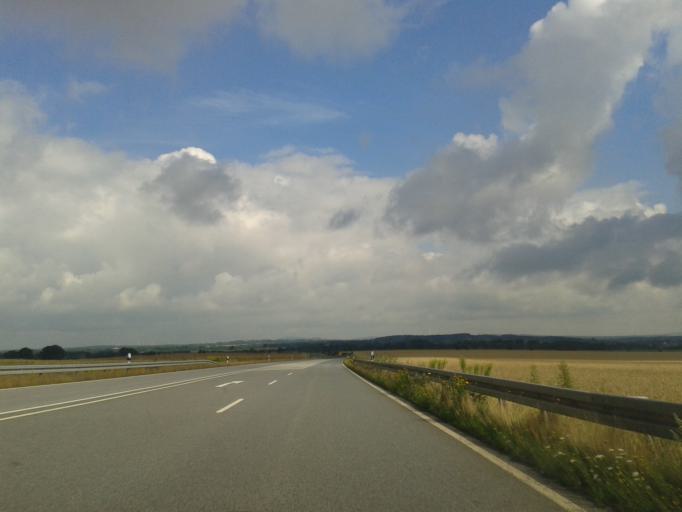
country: DE
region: Saxony
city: Radeberg
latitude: 51.0915
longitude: 13.9381
